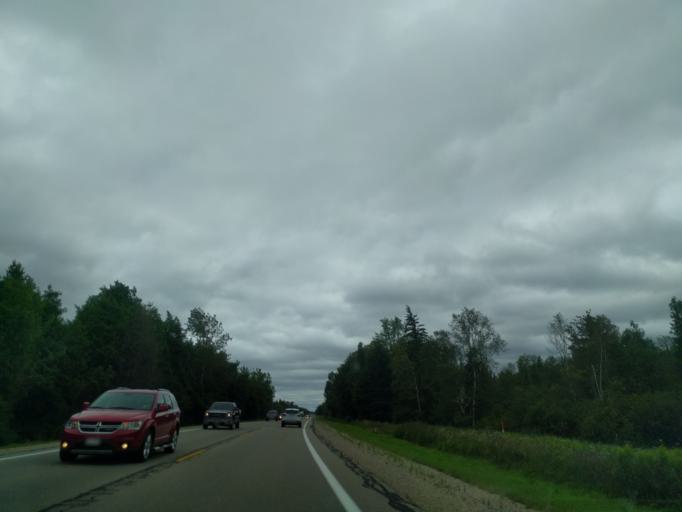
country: US
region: Michigan
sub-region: Delta County
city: Escanaba
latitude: 45.5046
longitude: -87.2889
